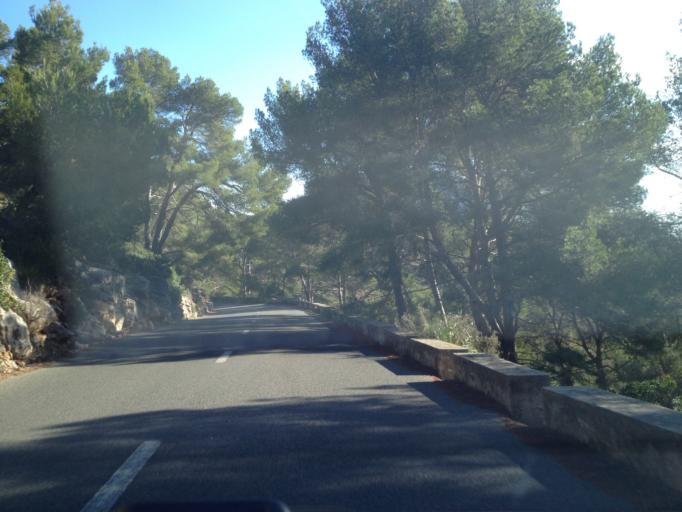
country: ES
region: Balearic Islands
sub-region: Illes Balears
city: Alcudia
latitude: 39.9319
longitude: 3.1238
